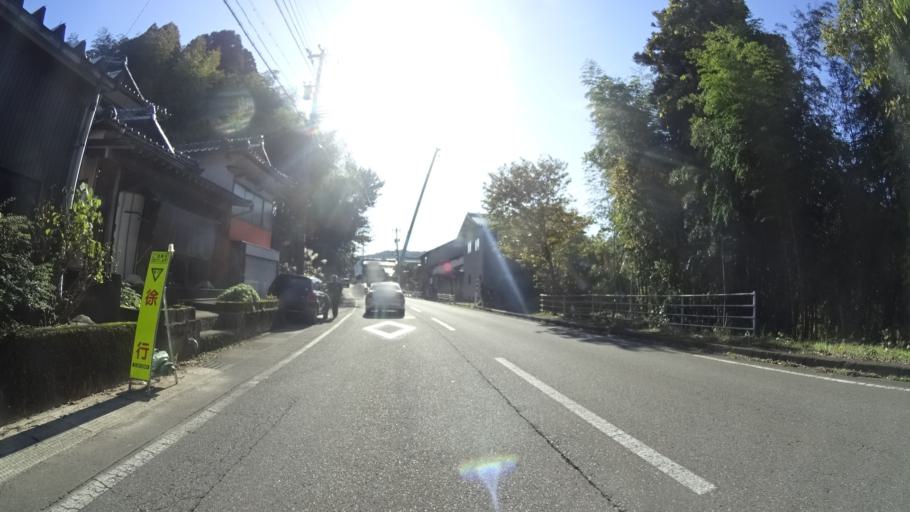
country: JP
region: Ishikawa
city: Komatsu
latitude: 36.3860
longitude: 136.5290
